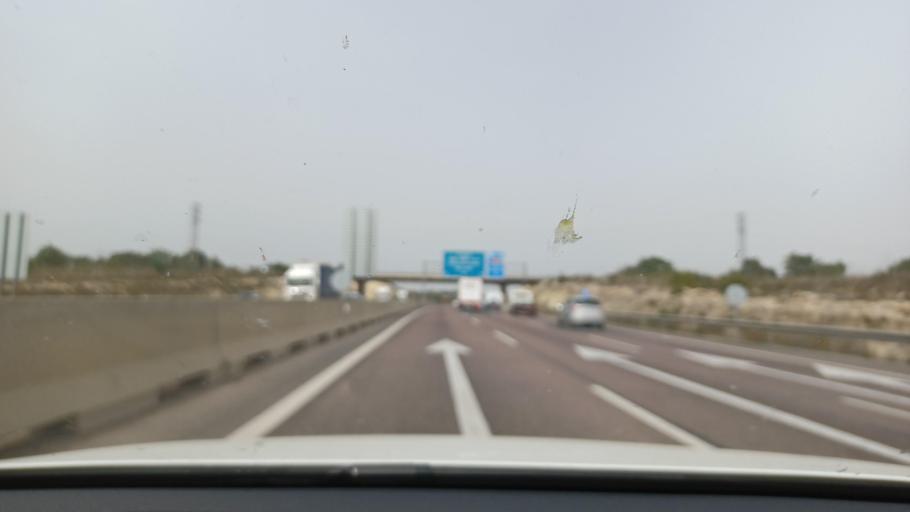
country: ES
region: Valencia
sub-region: Provincia de Valencia
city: Godella
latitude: 39.5343
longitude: -0.4597
